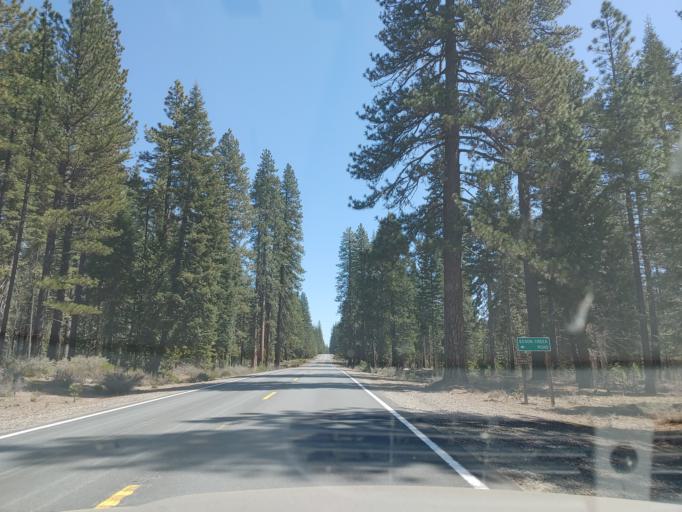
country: US
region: California
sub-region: Siskiyou County
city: McCloud
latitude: 41.2655
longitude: -121.9301
